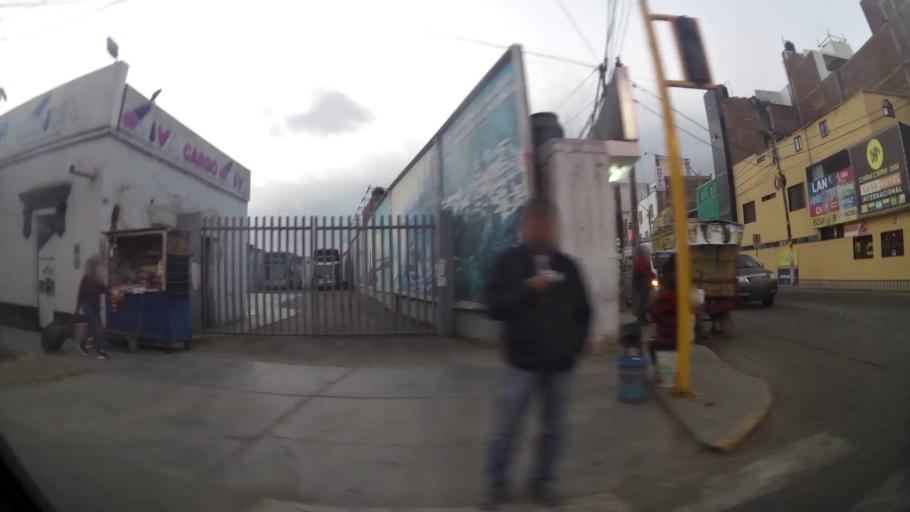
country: PE
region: La Libertad
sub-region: Provincia de Trujillo
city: Trujillo
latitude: -8.1043
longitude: -79.0231
